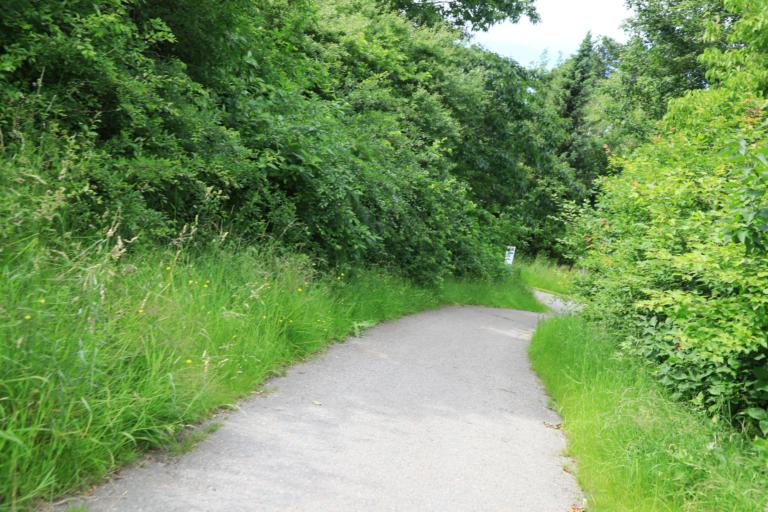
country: SE
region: Halland
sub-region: Varbergs Kommun
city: Varberg
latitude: 57.1149
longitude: 12.2761
